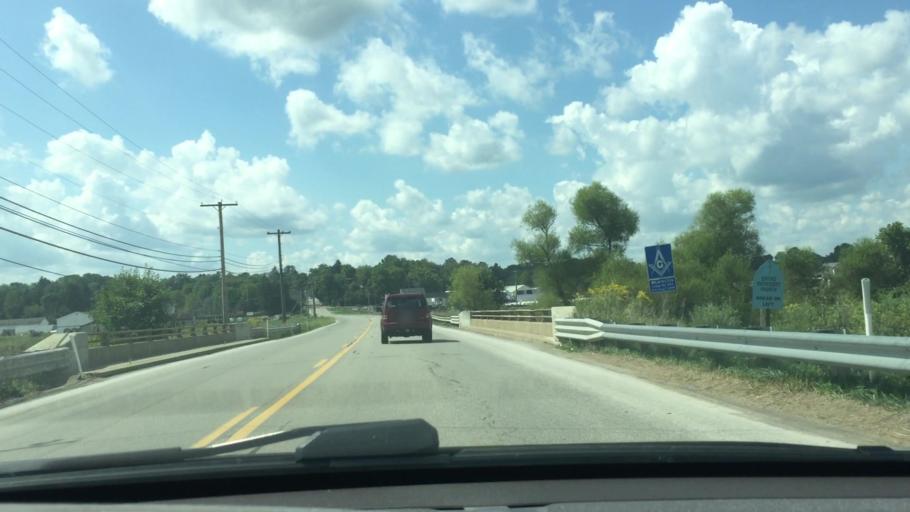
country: US
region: Pennsylvania
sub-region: Lawrence County
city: New Wilmington
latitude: 41.1227
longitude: -80.3206
